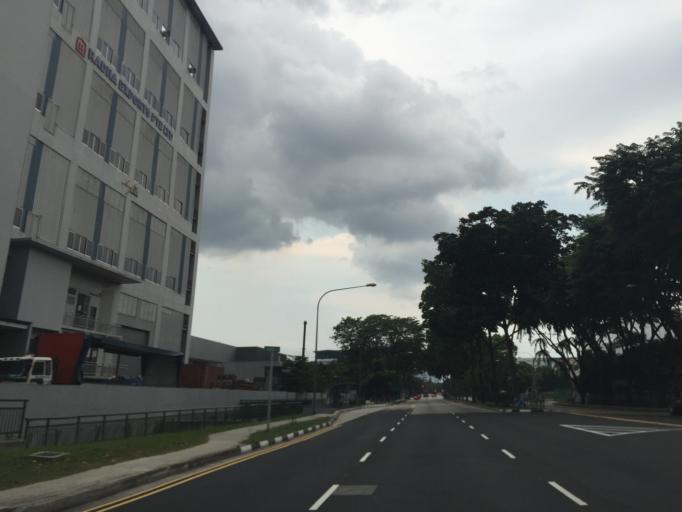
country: MY
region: Johor
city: Johor Bahru
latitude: 1.3308
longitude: 103.6966
